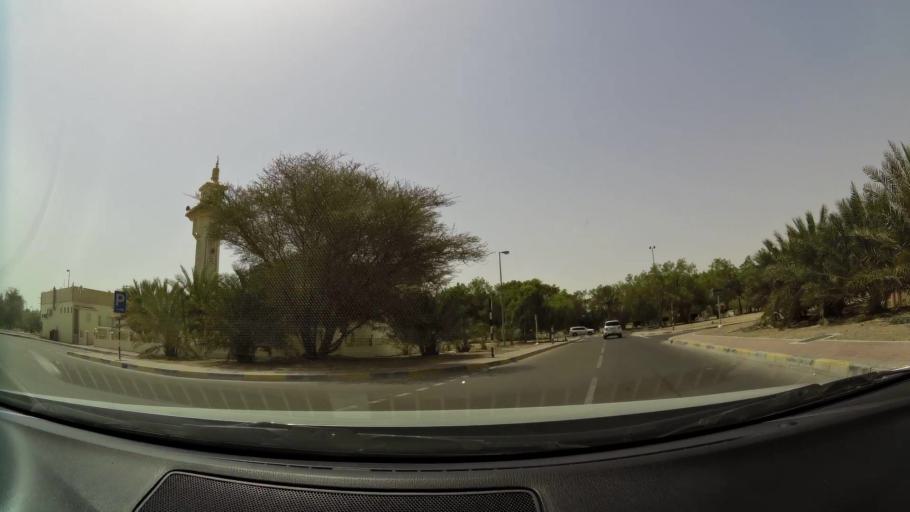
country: AE
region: Abu Dhabi
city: Al Ain
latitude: 24.1751
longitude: 55.7195
